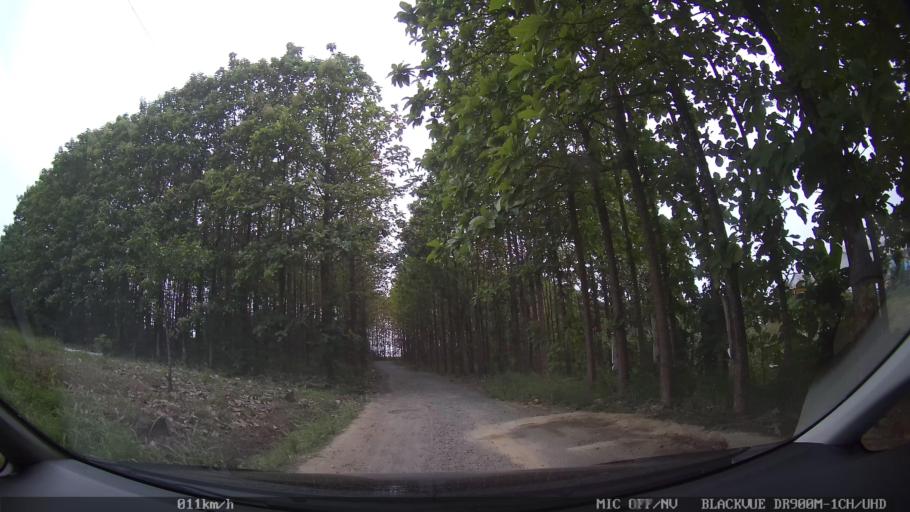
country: ID
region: Lampung
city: Panjang
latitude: -5.4031
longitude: 105.3566
